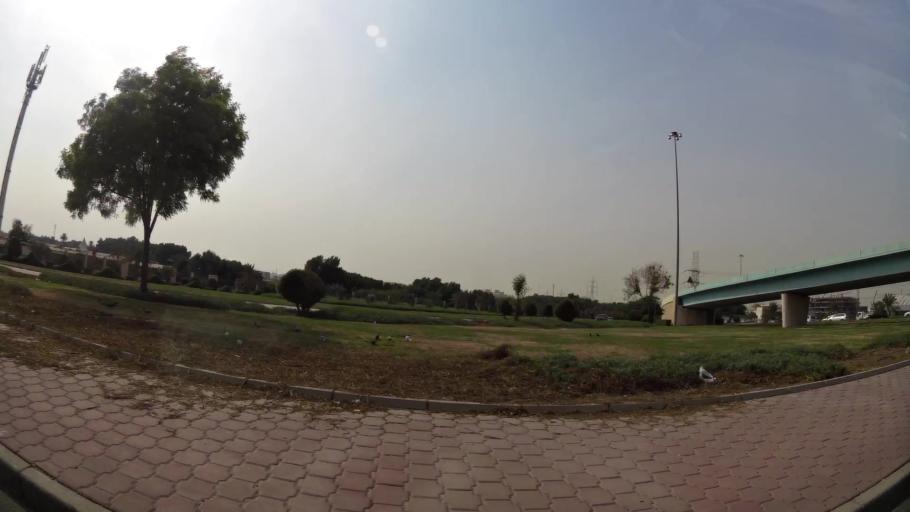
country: KW
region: Al Asimah
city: Ar Rabiyah
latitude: 29.2994
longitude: 47.9456
